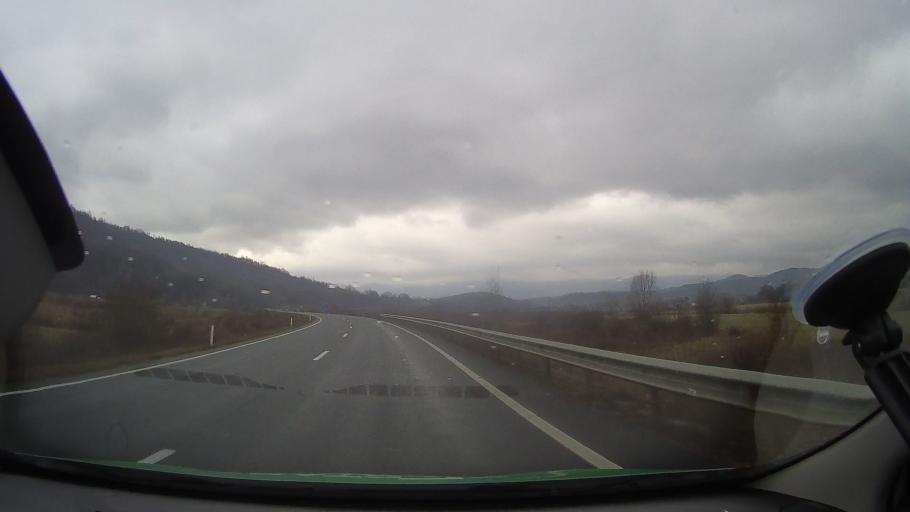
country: RO
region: Hunedoara
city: Vata de Jos
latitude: 46.2151
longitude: 22.5770
